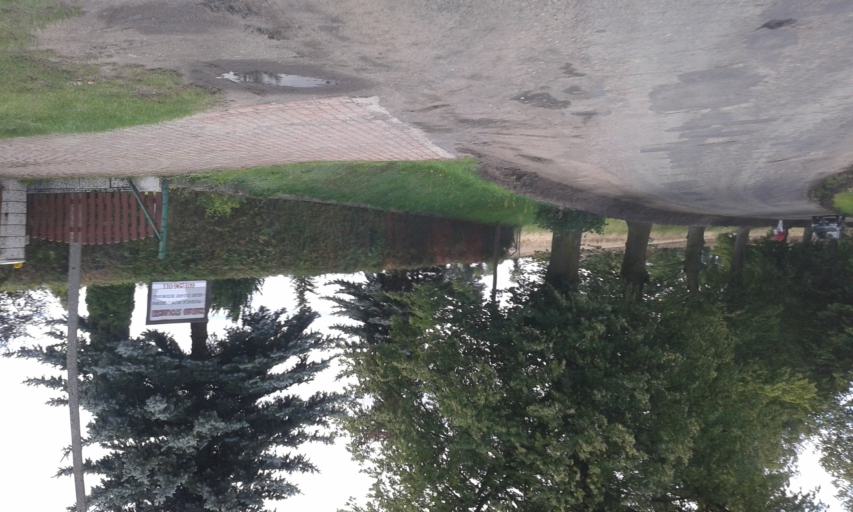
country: PL
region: Greater Poland Voivodeship
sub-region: Powiat pilski
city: Szydlowo
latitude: 53.2077
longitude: 16.5867
